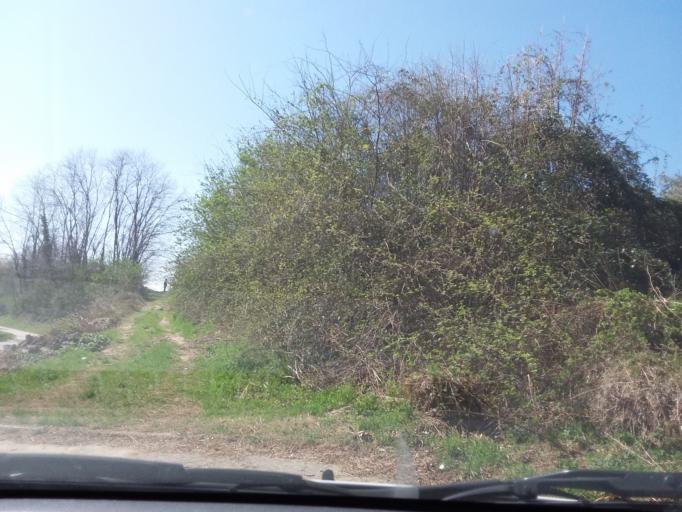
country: IT
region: Piedmont
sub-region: Provincia di Torino
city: Rivoli
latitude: 45.0581
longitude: 7.5157
